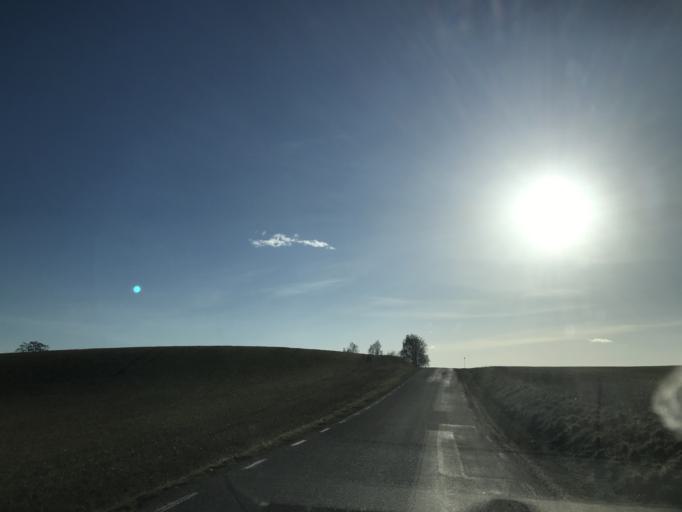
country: SE
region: Skane
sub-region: Ystads Kommun
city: Ystad
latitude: 55.5374
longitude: 13.7876
